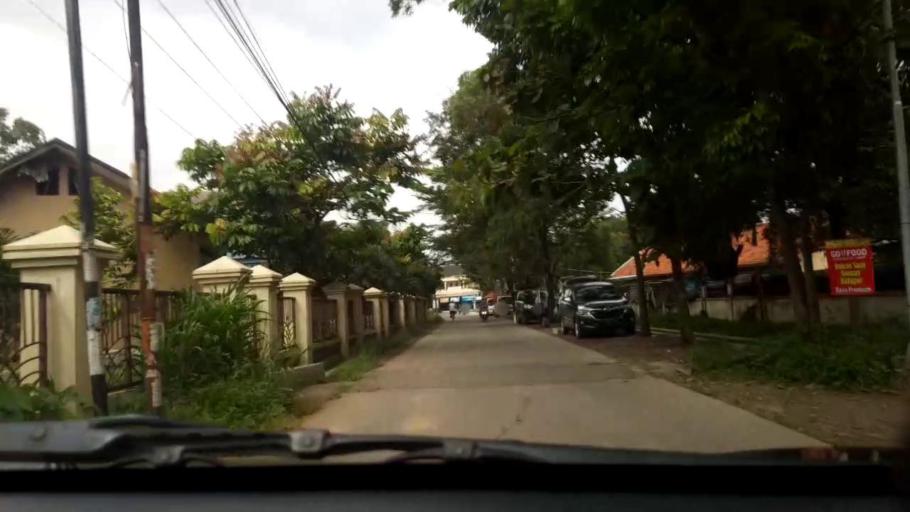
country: ID
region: West Java
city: Cileunyi
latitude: -6.9404
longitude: 107.7245
